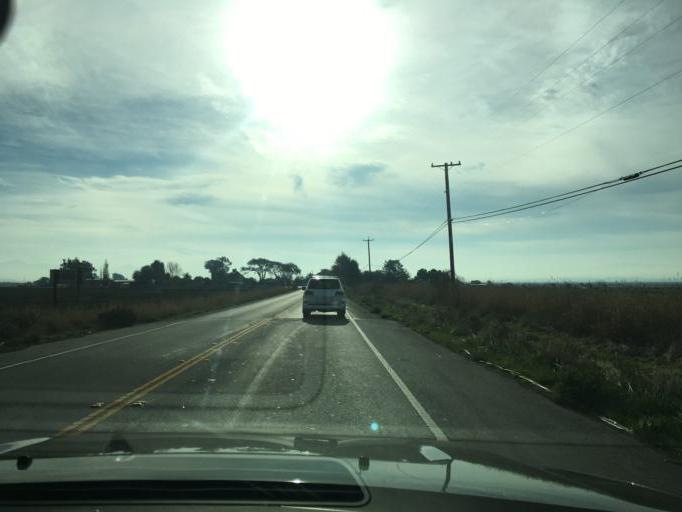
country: US
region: California
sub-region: Santa Clara County
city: Gilroy
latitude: 36.9925
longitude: -121.4970
